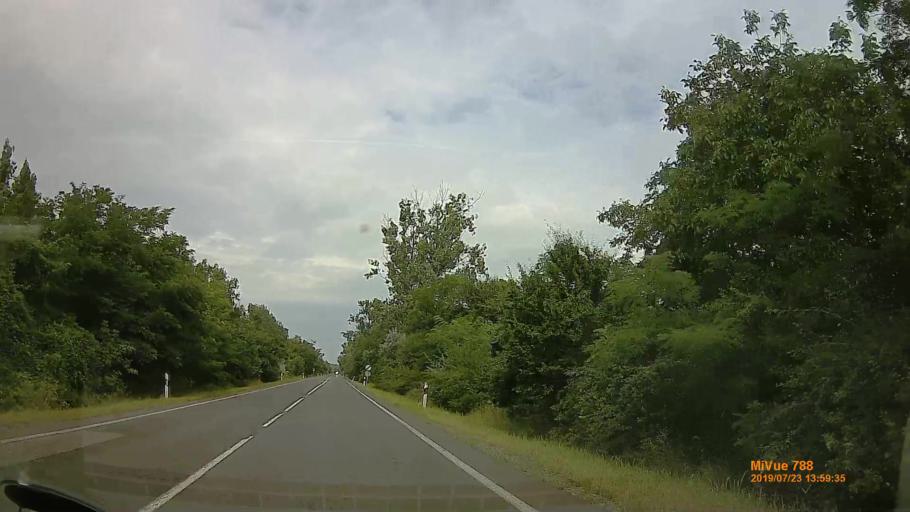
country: HU
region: Szabolcs-Szatmar-Bereg
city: Tiszavasvari
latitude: 47.9276
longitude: 21.2958
